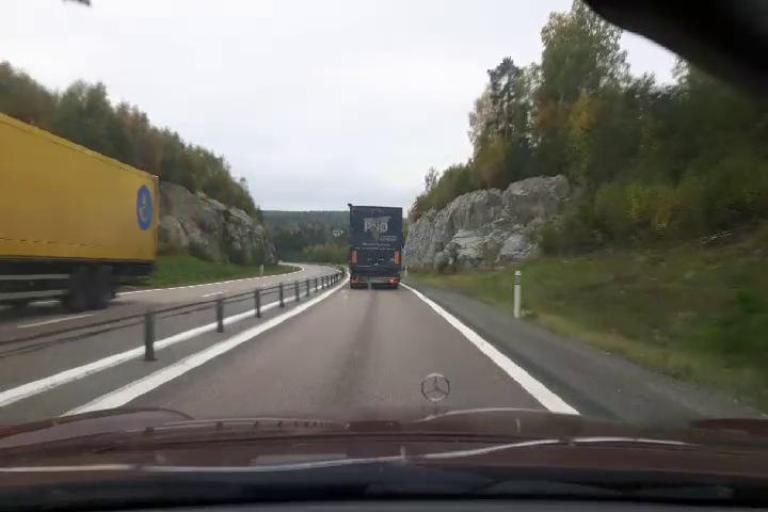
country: SE
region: Vaesternorrland
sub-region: Haernoesands Kommun
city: Haernoesand
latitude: 62.8358
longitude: 17.9683
